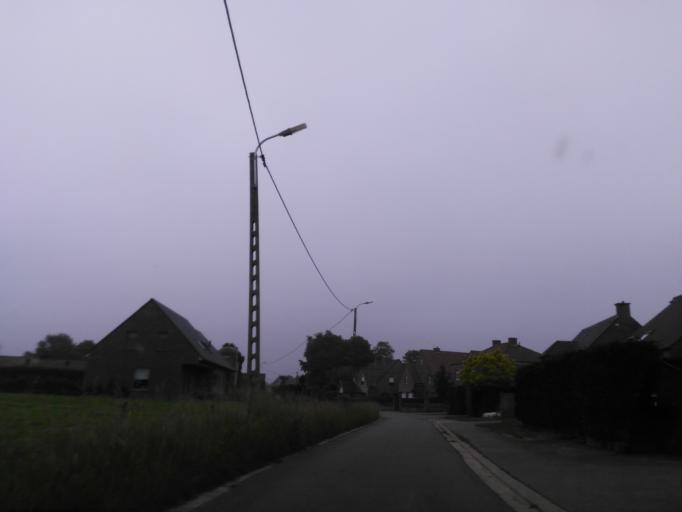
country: BE
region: Flanders
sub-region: Provincie Oost-Vlaanderen
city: Sint-Gillis-Waas
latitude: 51.2263
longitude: 4.1858
